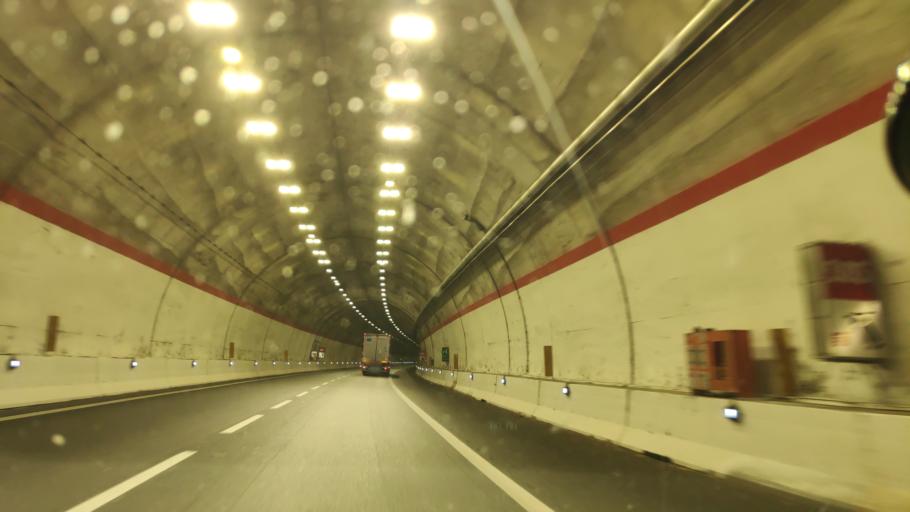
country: IT
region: Campania
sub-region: Provincia di Salerno
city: Sicignano degli Alburni
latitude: 40.5823
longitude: 15.3424
